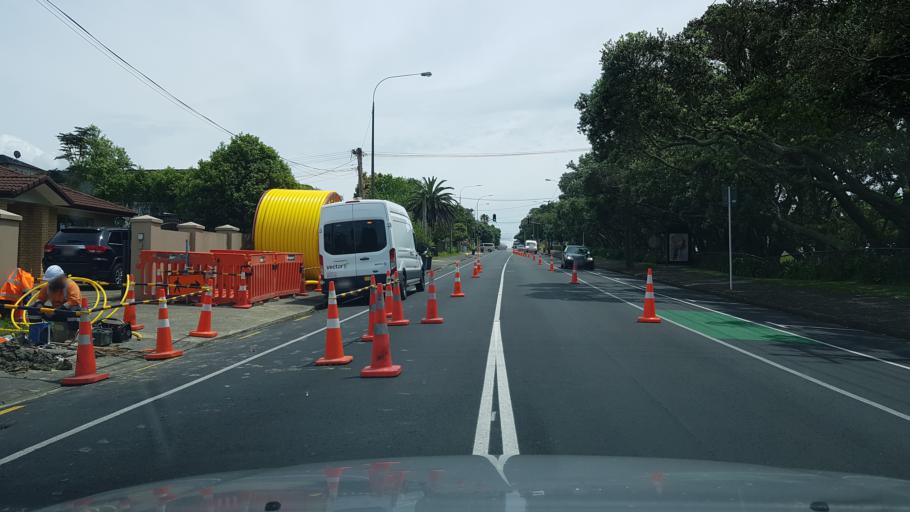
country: NZ
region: Auckland
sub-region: Auckland
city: North Shore
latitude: -36.8026
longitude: 174.7874
